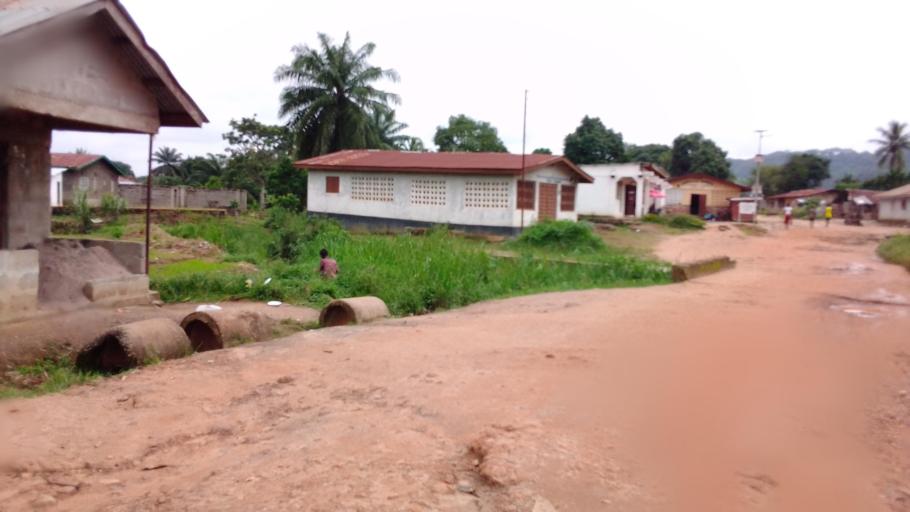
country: SL
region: Eastern Province
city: Kenema
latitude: 7.8721
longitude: -11.2003
